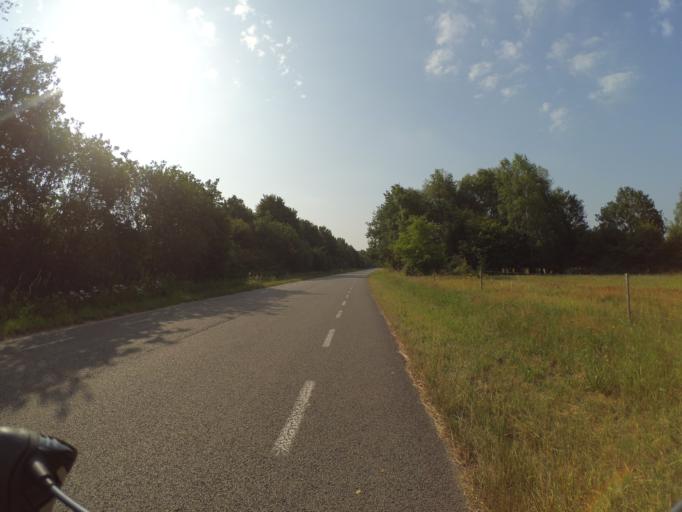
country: NL
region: North Brabant
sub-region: Gemeente Loon op Zand
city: Loon op Zand
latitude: 51.6131
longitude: 5.0579
